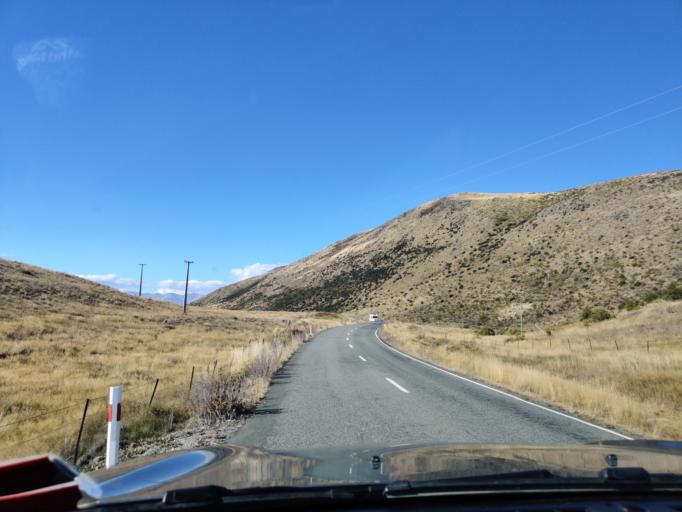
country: NZ
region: Canterbury
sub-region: Timaru District
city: Pleasant Point
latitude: -43.9892
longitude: 170.4516
